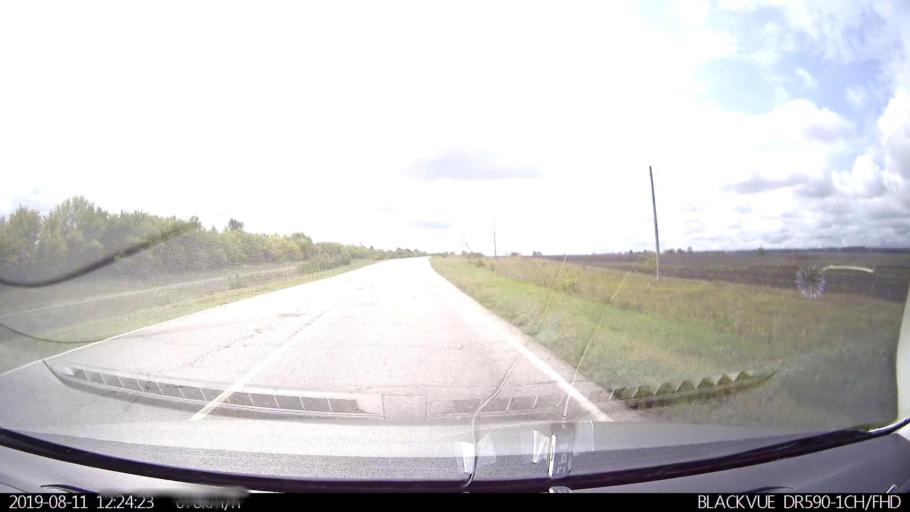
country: RU
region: Ulyanovsk
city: Ignatovka
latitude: 53.8840
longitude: 47.9490
